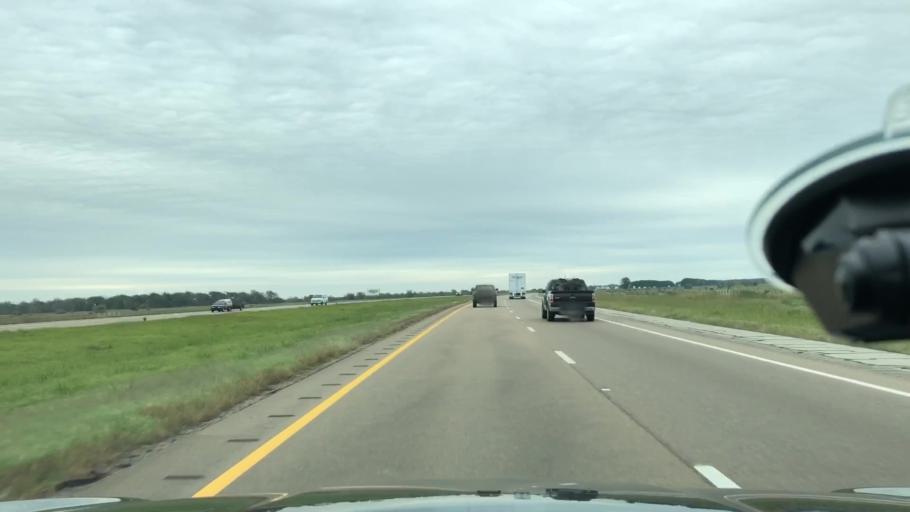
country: US
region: Texas
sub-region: Morris County
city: Omaha
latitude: 33.2878
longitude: -94.7841
